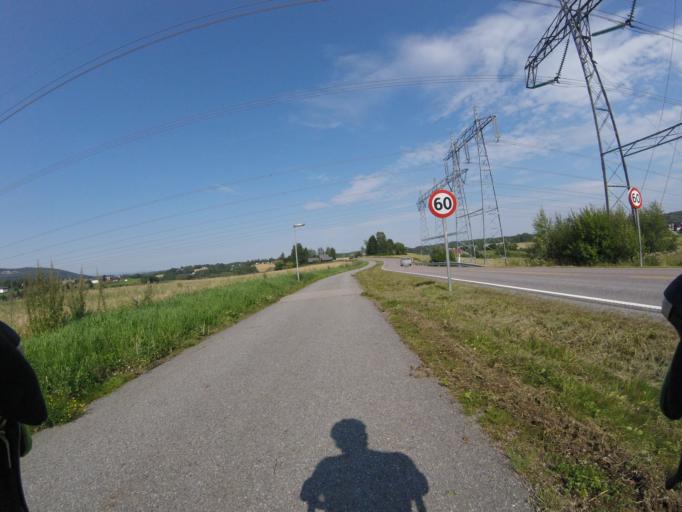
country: NO
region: Akershus
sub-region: Sorum
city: Frogner
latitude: 60.0058
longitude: 11.1046
